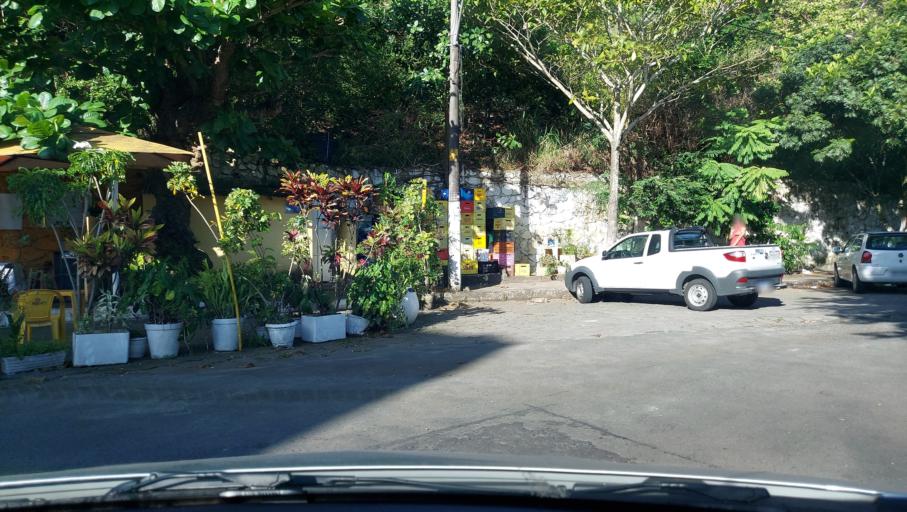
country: BR
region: Bahia
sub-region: Salvador
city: Salvador
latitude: -12.9769
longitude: -38.4472
